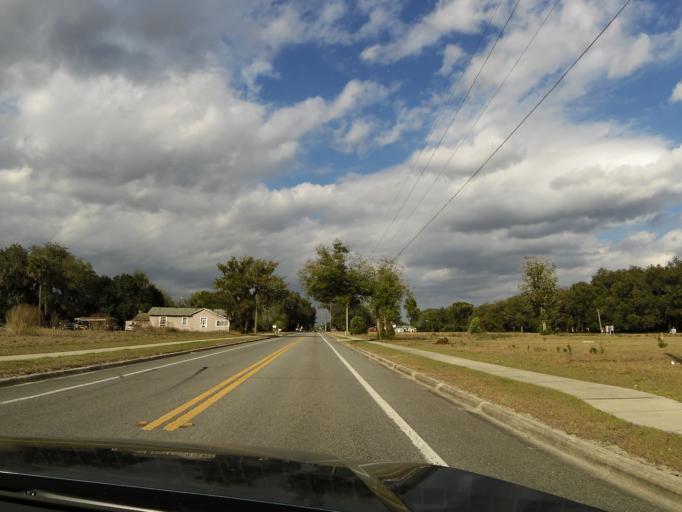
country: US
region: Florida
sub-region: Volusia County
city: Pierson
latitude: 29.2367
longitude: -81.4628
